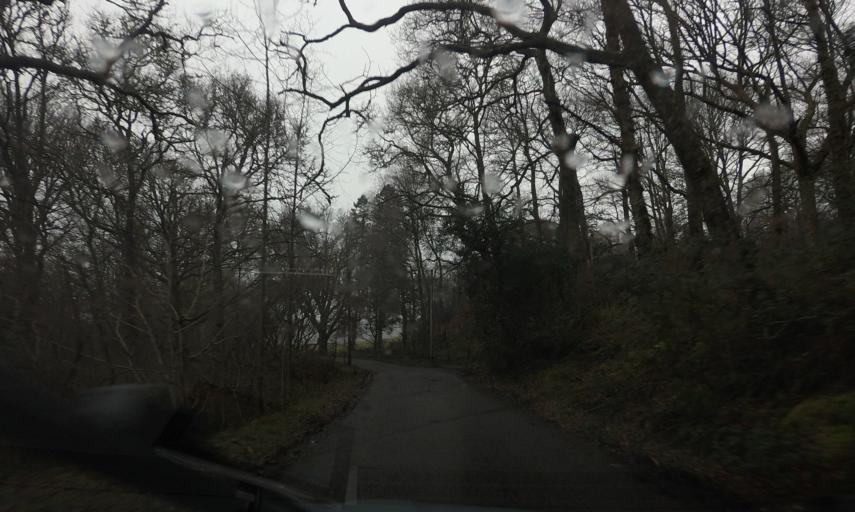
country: GB
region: Scotland
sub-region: West Dunbartonshire
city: Balloch
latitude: 56.1357
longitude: -4.6129
